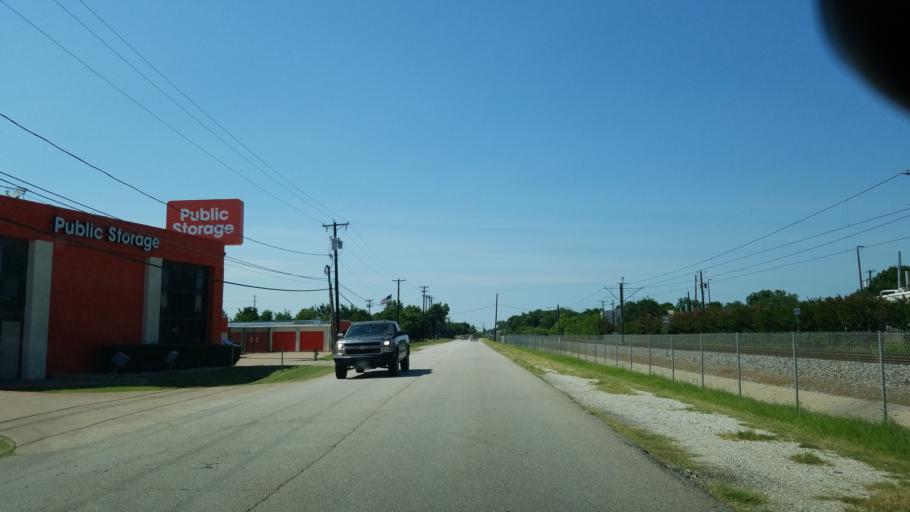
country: US
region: Texas
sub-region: Dallas County
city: Farmers Branch
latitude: 32.9127
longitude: -96.8937
